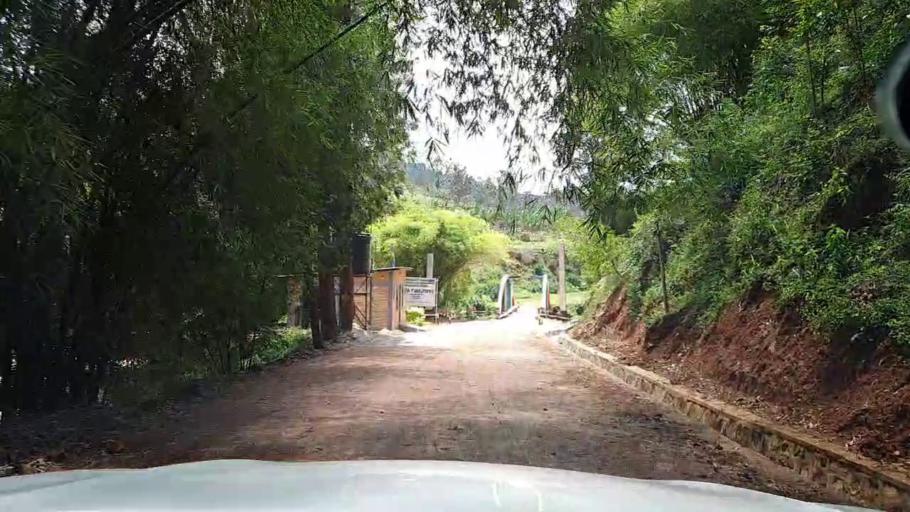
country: BI
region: Ngozi
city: Ngozi
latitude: -2.8151
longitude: 29.7276
